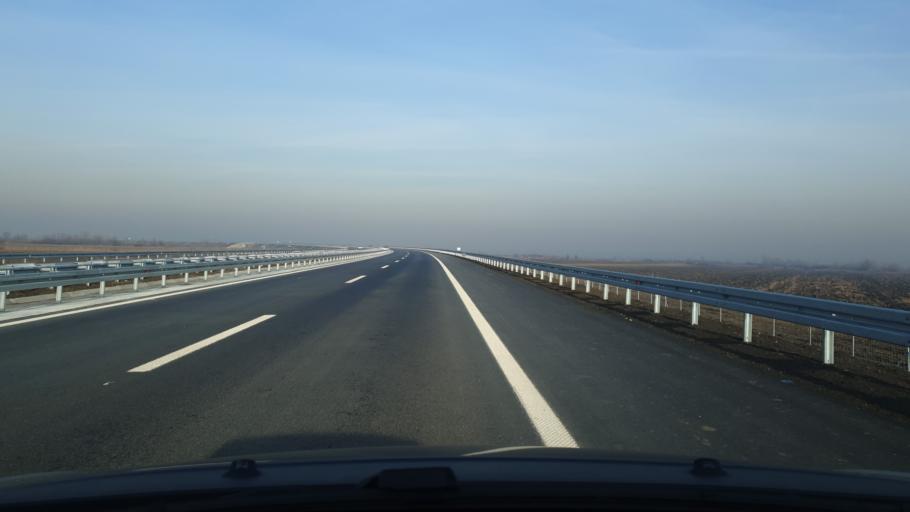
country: RS
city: Baric
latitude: 44.6829
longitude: 20.2636
